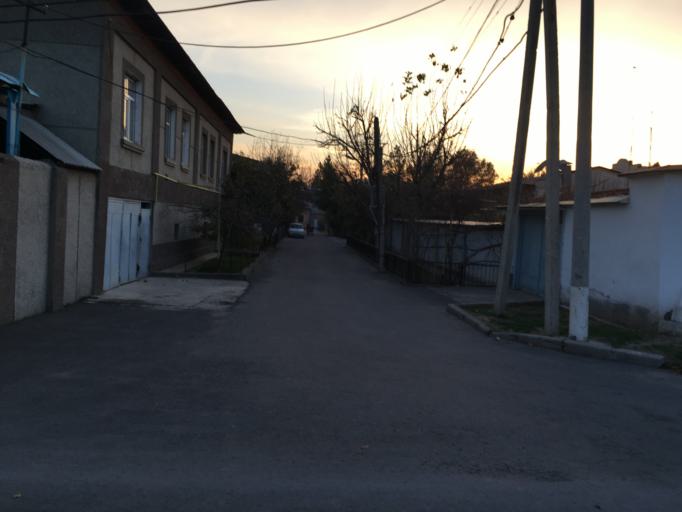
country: UZ
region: Toshkent
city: Salor
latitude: 41.3282
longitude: 69.3559
